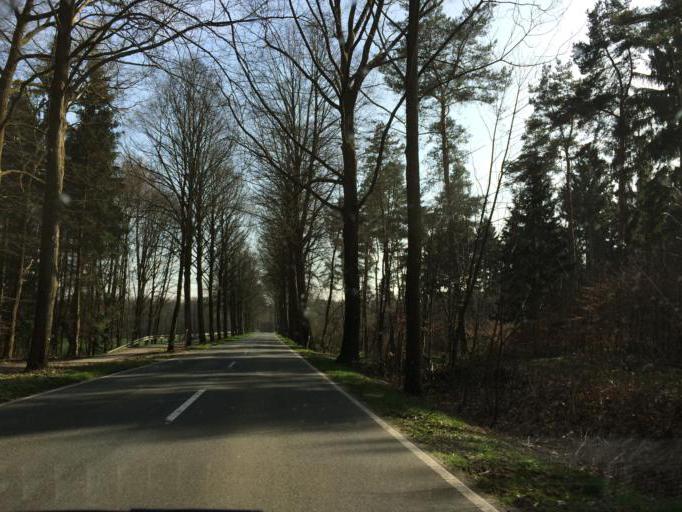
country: DE
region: North Rhine-Westphalia
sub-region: Regierungsbezirk Munster
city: Klein Reken
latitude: 51.7515
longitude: 7.1067
